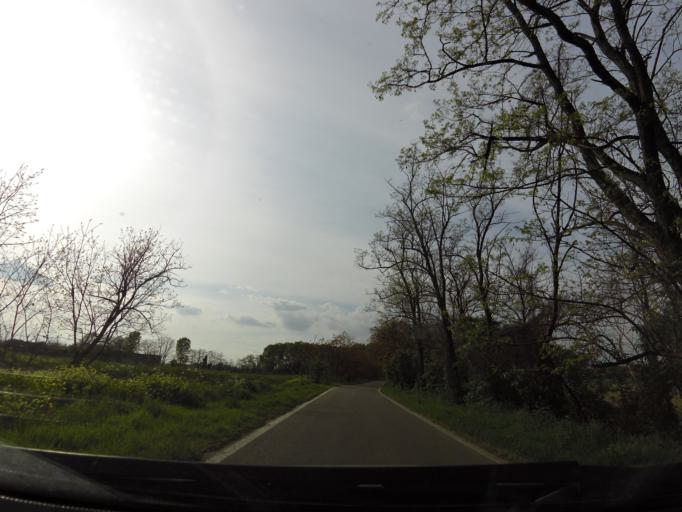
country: IT
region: Lombardy
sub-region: Citta metropolitana di Milano
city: Civesio
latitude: 45.3893
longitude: 9.2698
